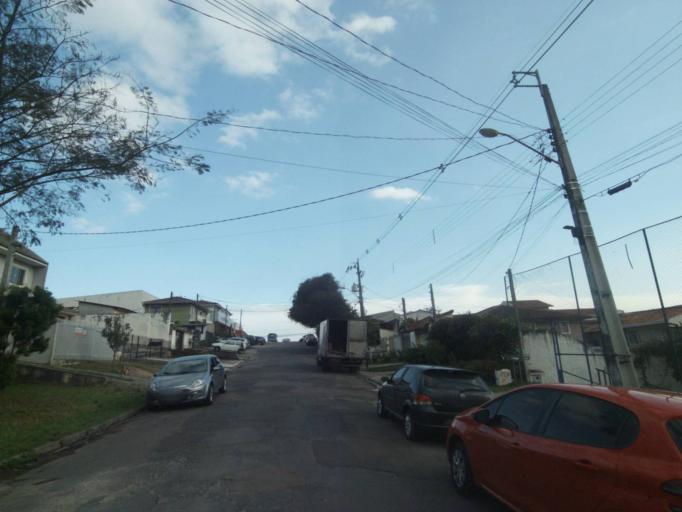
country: BR
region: Parana
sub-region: Pinhais
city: Pinhais
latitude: -25.4051
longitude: -49.2020
